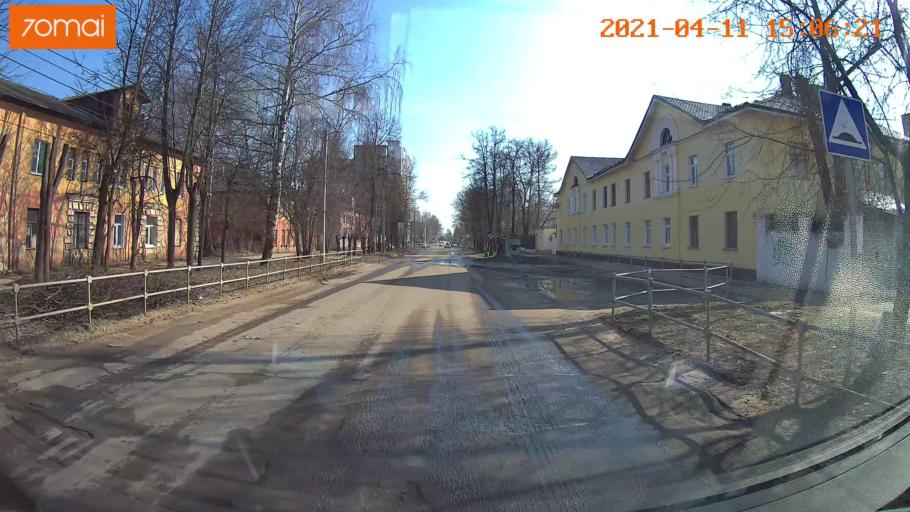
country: RU
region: Ivanovo
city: Bogorodskoye
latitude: 57.0192
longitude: 41.0164
